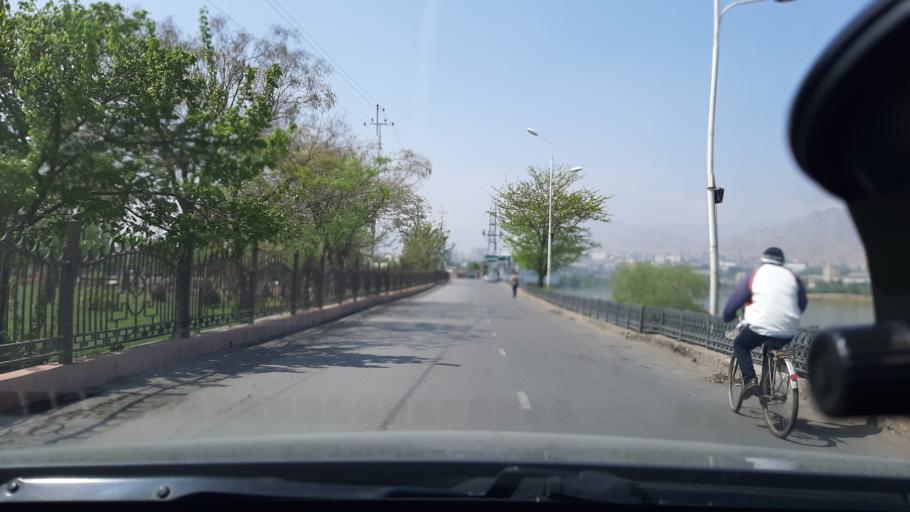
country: TJ
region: Viloyati Sughd
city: Khujand
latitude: 40.2882
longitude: 69.6153
